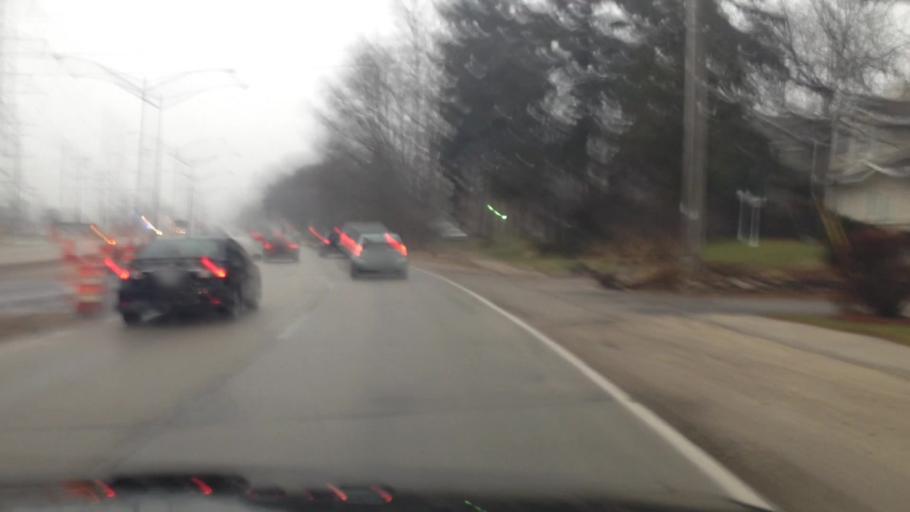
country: US
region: Wisconsin
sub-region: Milwaukee County
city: Hales Corners
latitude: 42.9345
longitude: -88.0504
